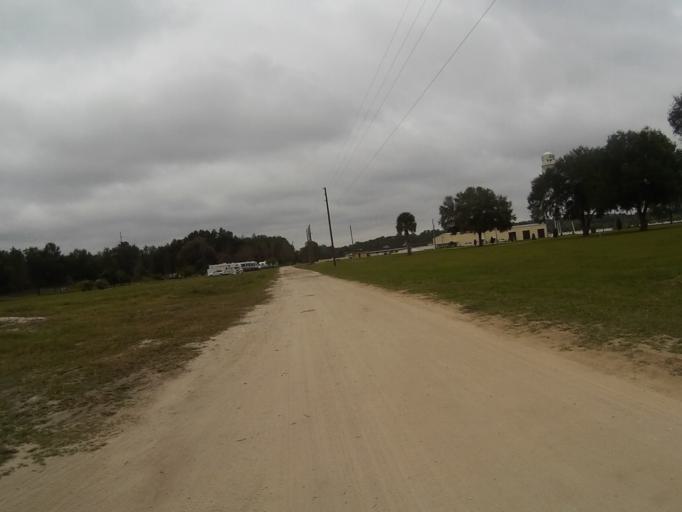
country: US
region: Florida
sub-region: Lake County
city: Umatilla
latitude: 28.9622
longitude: -81.6588
